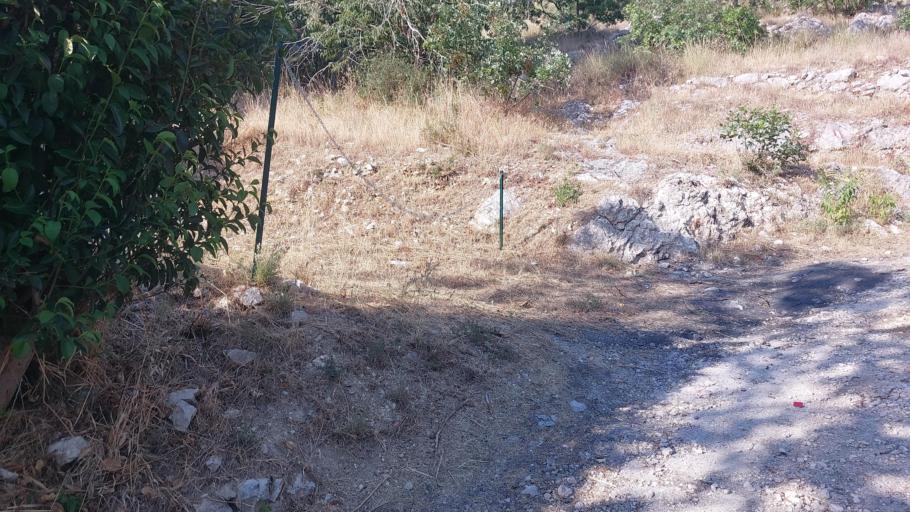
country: IT
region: Umbria
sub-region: Provincia di Perugia
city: Campello sul Clitunno
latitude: 42.8427
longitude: 12.7600
